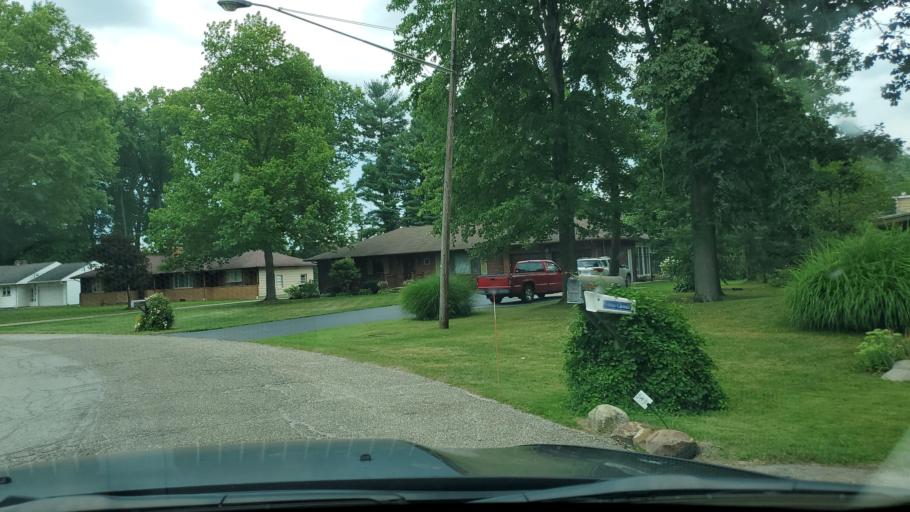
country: US
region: Ohio
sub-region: Trumbull County
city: Bolindale
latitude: 41.2315
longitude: -80.7666
